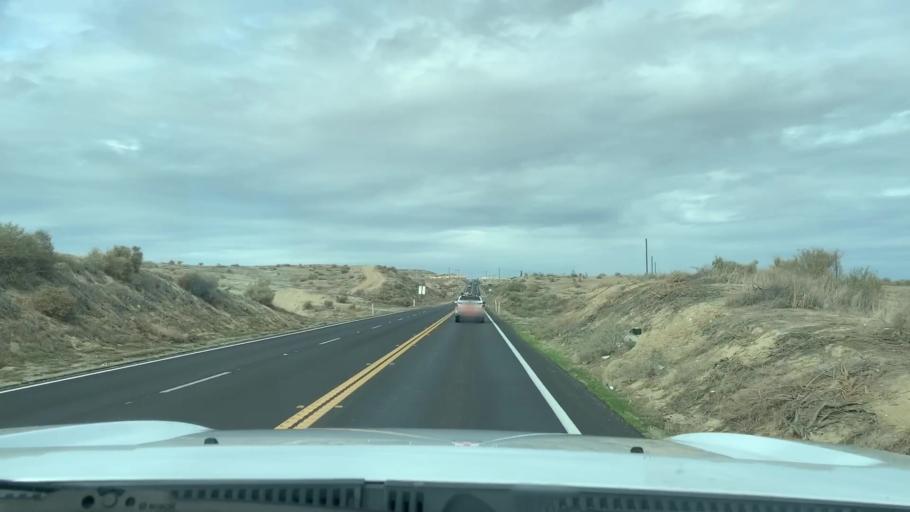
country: US
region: California
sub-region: Kern County
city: South Taft
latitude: 35.1091
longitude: -119.4236
